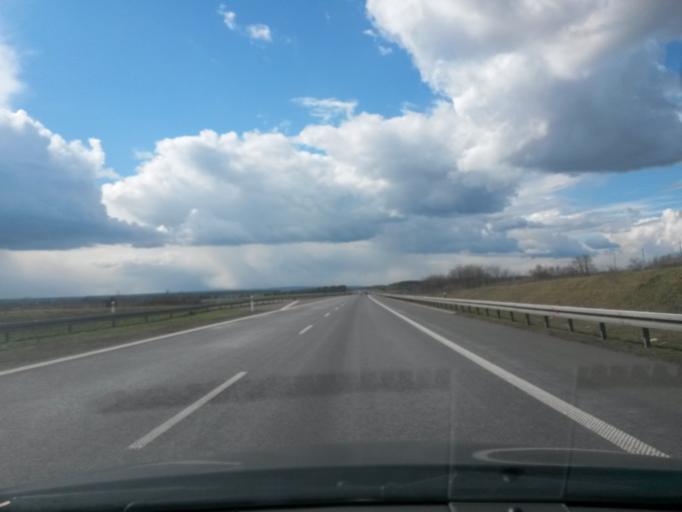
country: PL
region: Greater Poland Voivodeship
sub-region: Powiat turecki
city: Wladyslawow
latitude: 52.1455
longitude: 18.5113
